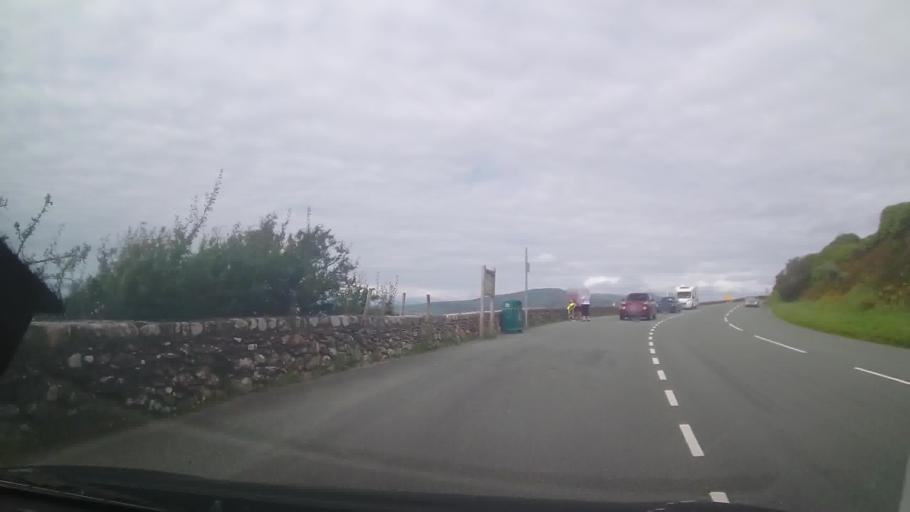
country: GB
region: Wales
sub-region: Gwynedd
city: Barmouth
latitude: 52.6791
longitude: -4.0716
